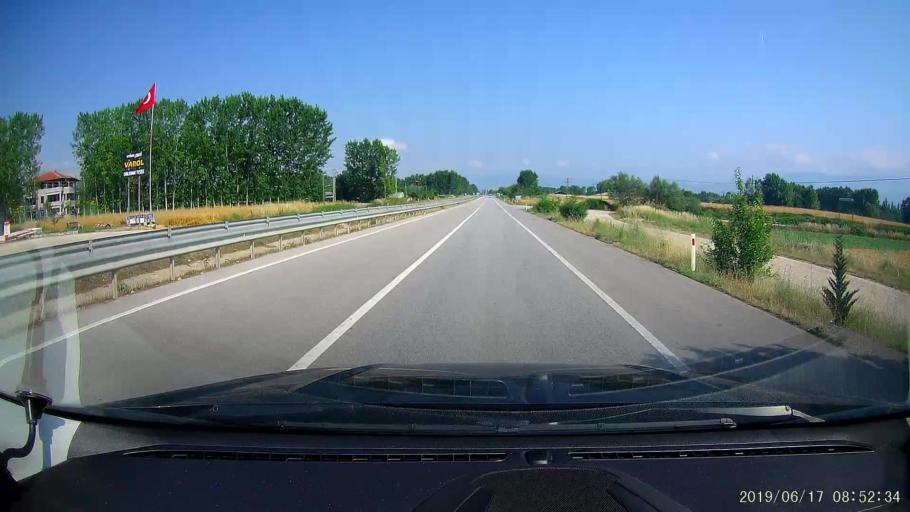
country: TR
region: Tokat
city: Erbaa
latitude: 40.6995
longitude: 36.4945
